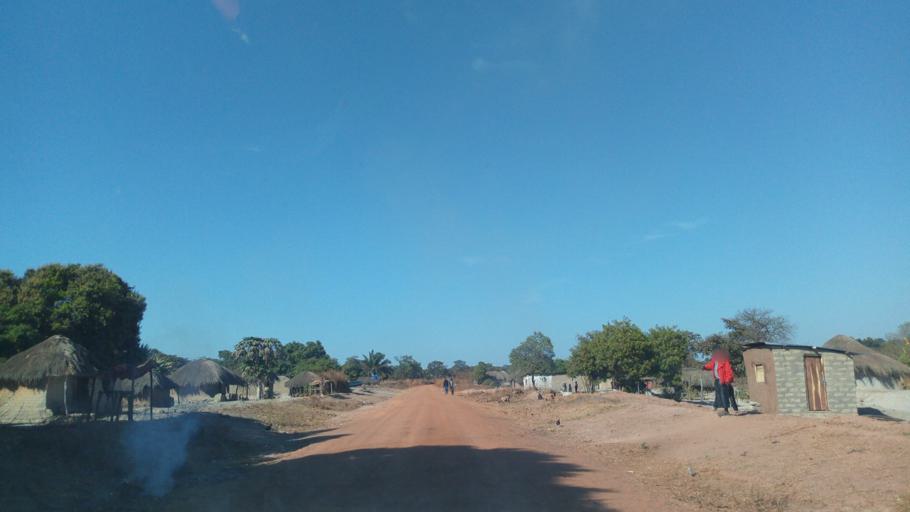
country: ZM
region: Luapula
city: Mwense
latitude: -10.6288
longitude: 28.4110
